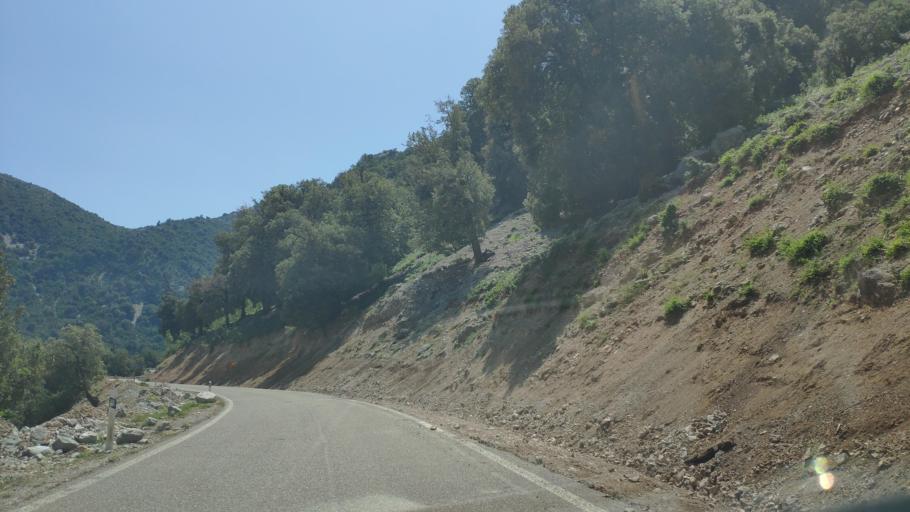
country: GR
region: West Greece
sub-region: Nomos Aitolias kai Akarnanias
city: Krikellos
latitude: 39.0182
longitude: 21.3478
